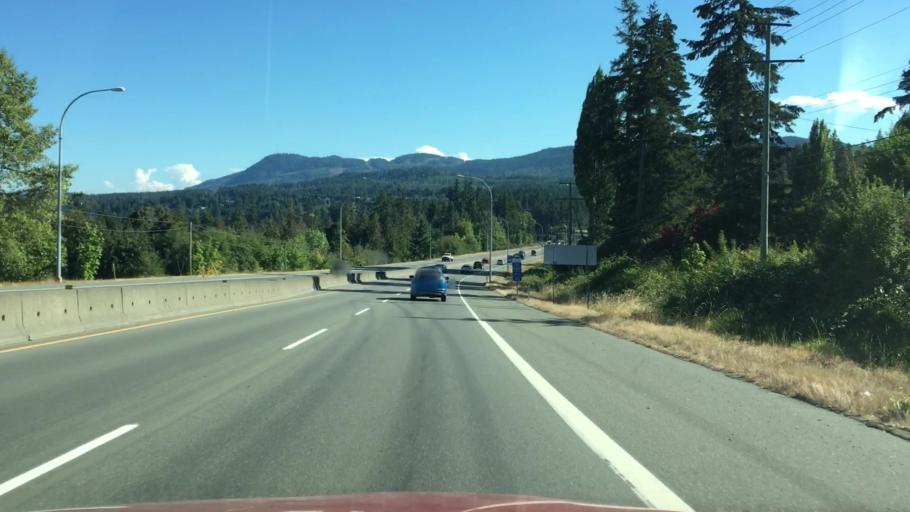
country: CA
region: British Columbia
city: North Saanich
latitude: 48.6630
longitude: -123.5596
